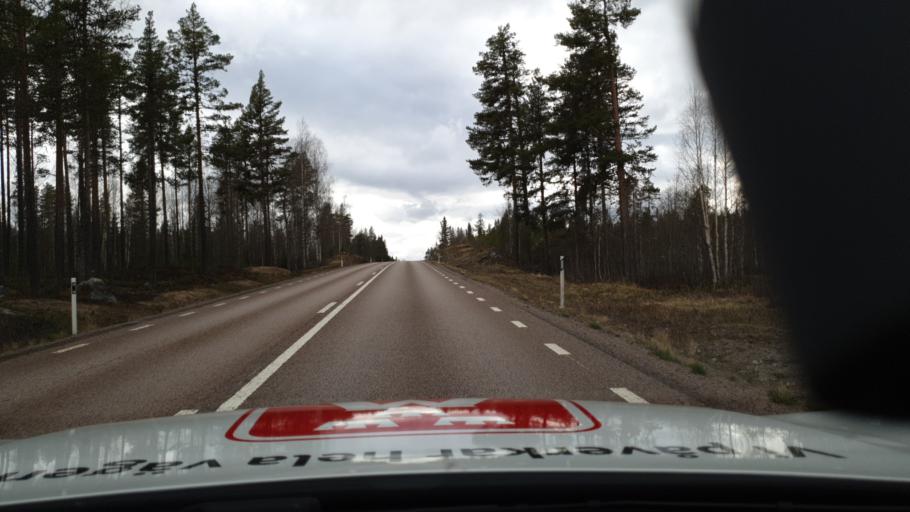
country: SE
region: Jaemtland
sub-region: OEstersunds Kommun
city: Brunflo
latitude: 63.1926
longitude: 15.2708
